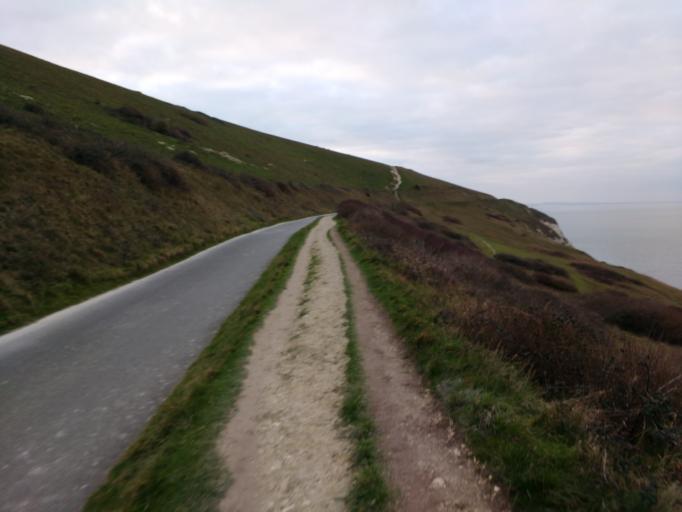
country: GB
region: England
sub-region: Isle of Wight
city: Totland
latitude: 50.6641
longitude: -1.5712
